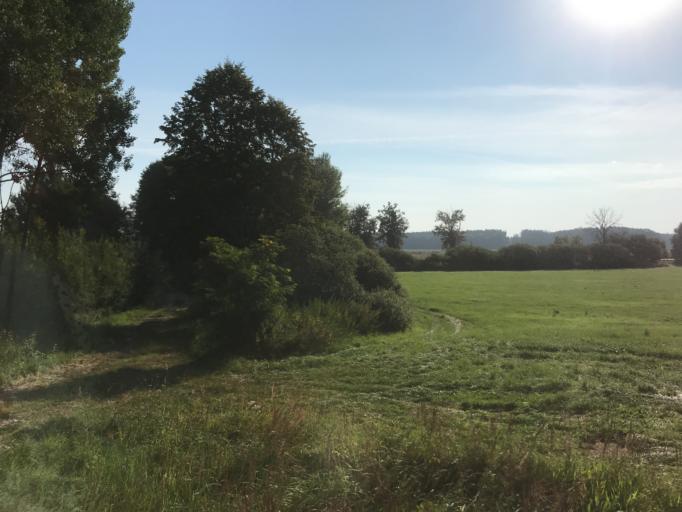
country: CZ
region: Jihocesky
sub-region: Okres Jindrichuv Hradec
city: Lomnice nad Luznici
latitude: 49.0732
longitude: 14.7303
